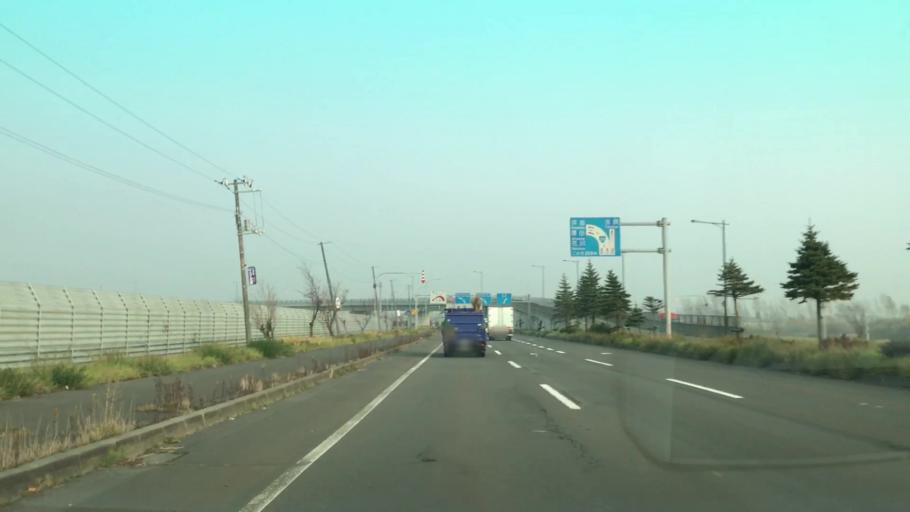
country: JP
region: Hokkaido
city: Ishikari
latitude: 43.1768
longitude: 141.3481
